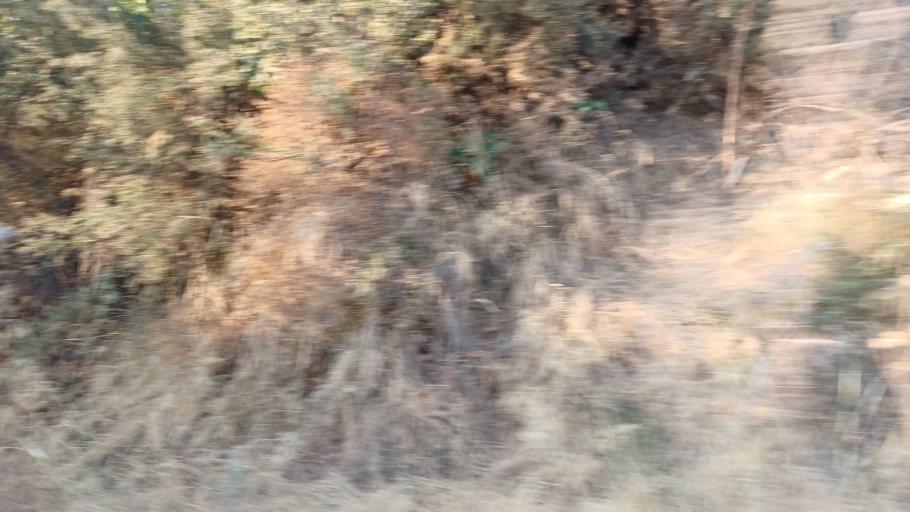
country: CY
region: Pafos
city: Polis
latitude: 35.0478
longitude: 32.4575
